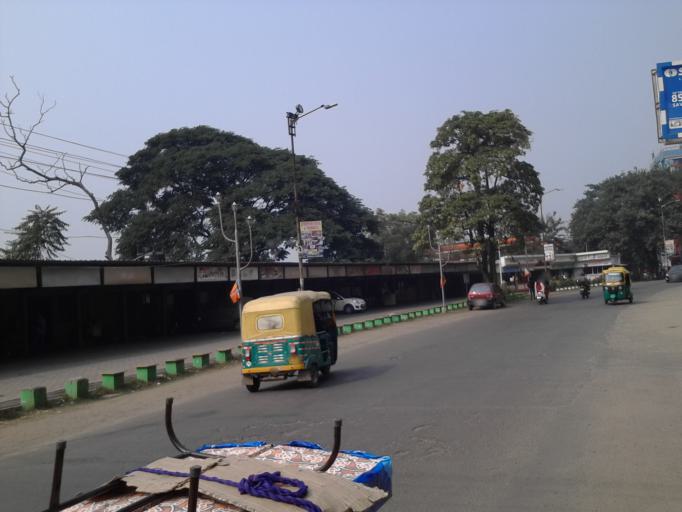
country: IN
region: West Bengal
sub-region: Barddhaman
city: Durgapur
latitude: 23.5367
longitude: 87.2946
